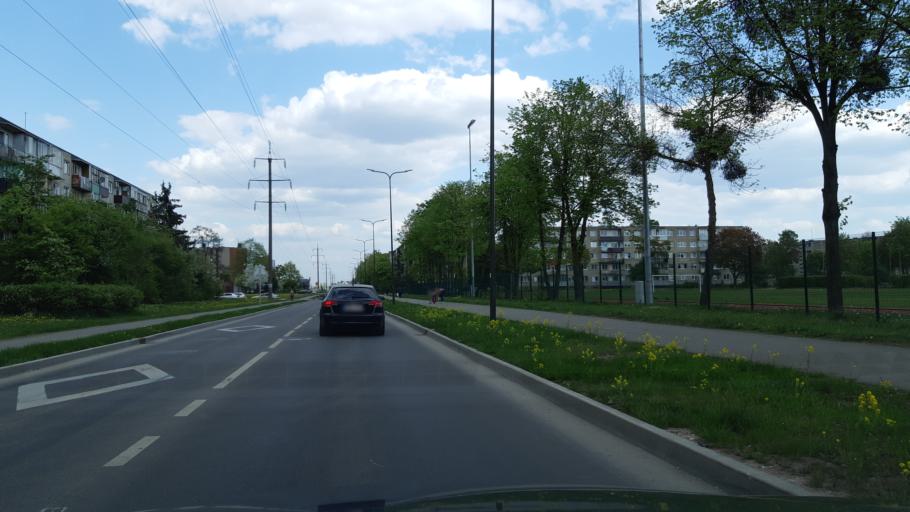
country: LT
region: Kauno apskritis
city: Dainava (Kaunas)
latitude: 54.9243
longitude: 23.9693
